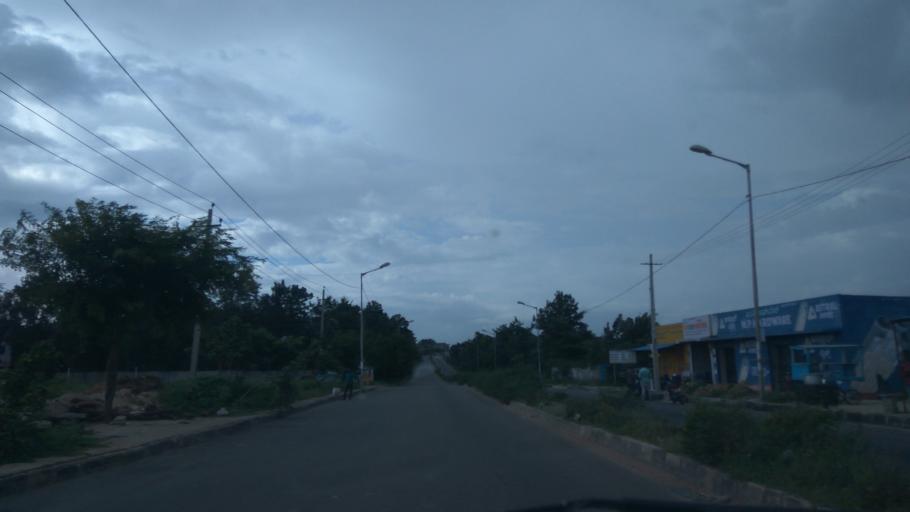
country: IN
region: Karnataka
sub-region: Bangalore Urban
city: Yelahanka
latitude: 13.1032
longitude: 77.6345
